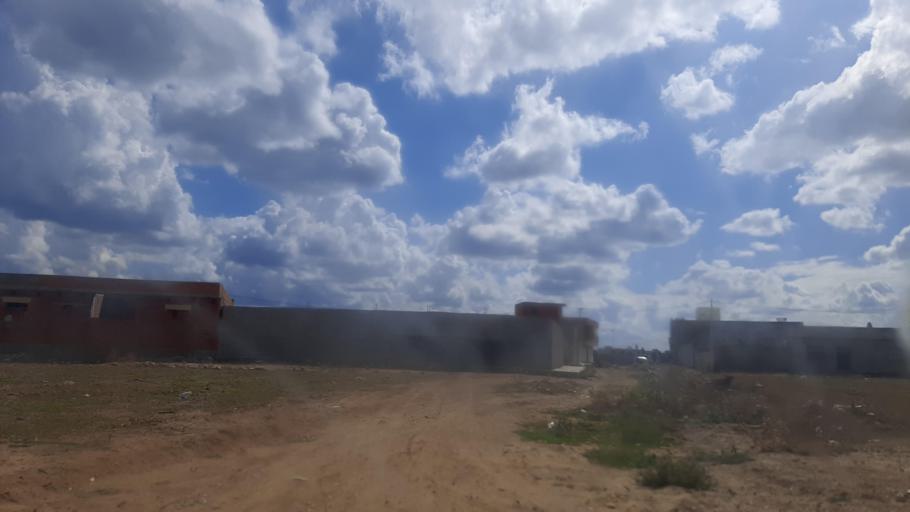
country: TN
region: Nabul
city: Korba
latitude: 36.5940
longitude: 10.8565
